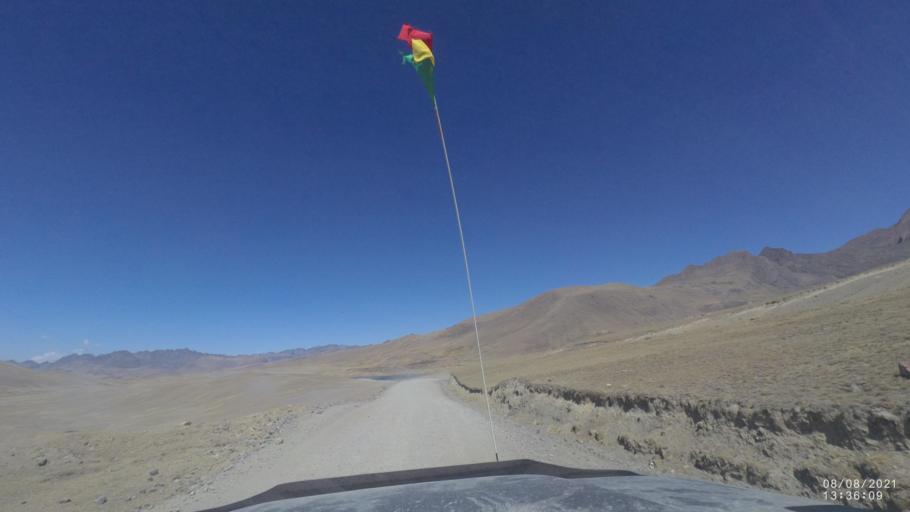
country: BO
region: Cochabamba
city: Colchani
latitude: -17.0710
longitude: -66.5036
